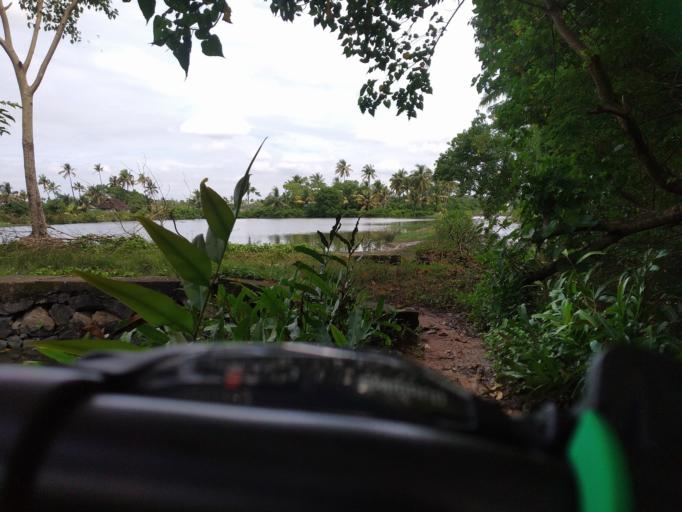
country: IN
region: Kerala
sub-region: Ernakulam
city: Elur
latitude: 10.0777
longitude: 76.2153
